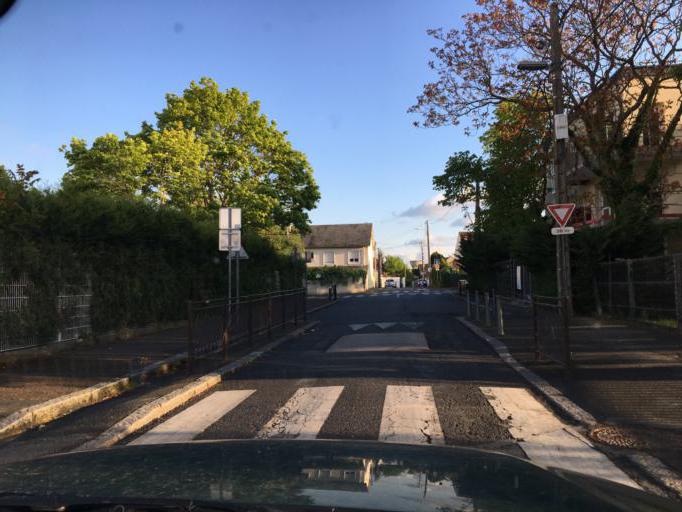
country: FR
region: Centre
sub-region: Departement du Loiret
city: Semoy
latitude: 47.9172
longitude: 1.9375
